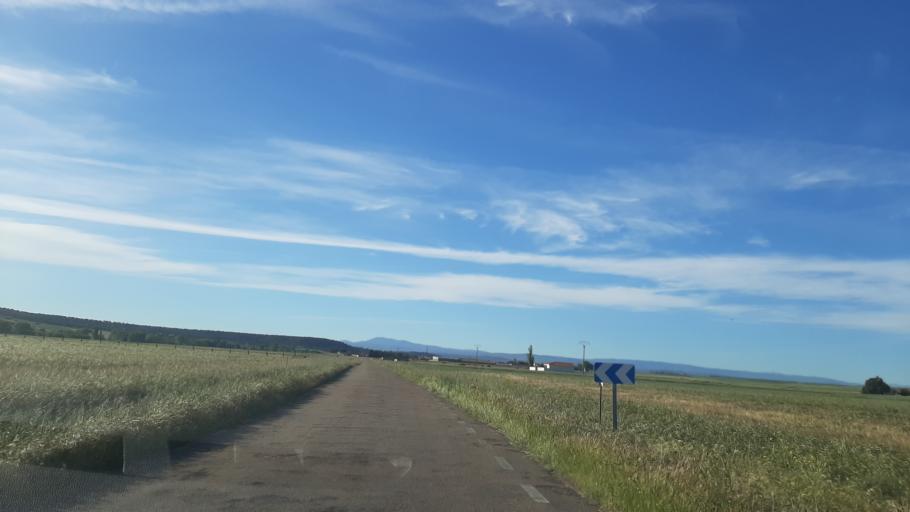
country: ES
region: Castille and Leon
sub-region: Provincia de Salamanca
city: Pedrosillo de Alba
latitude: 40.8161
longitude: -5.3893
